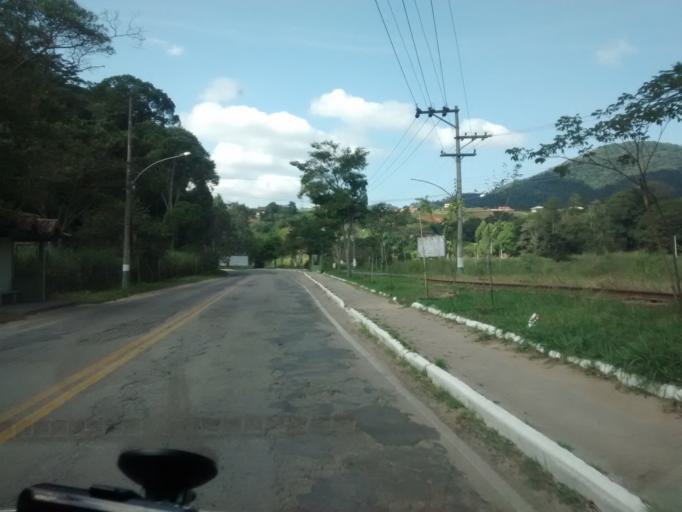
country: BR
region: Rio de Janeiro
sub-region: Miguel Pereira
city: Miguel Pereira
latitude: -22.4651
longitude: -43.4865
